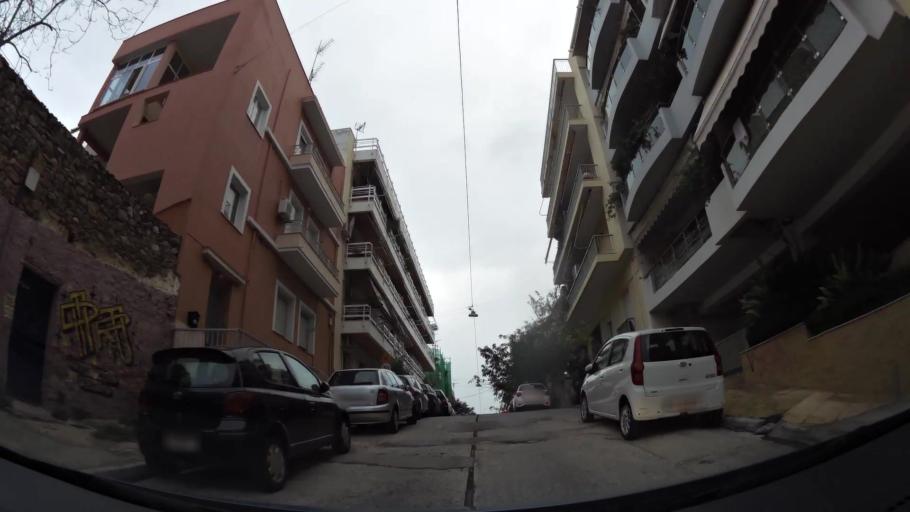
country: GR
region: Attica
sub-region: Nomarchia Athinas
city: Vyronas
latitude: 37.9646
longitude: 23.7412
